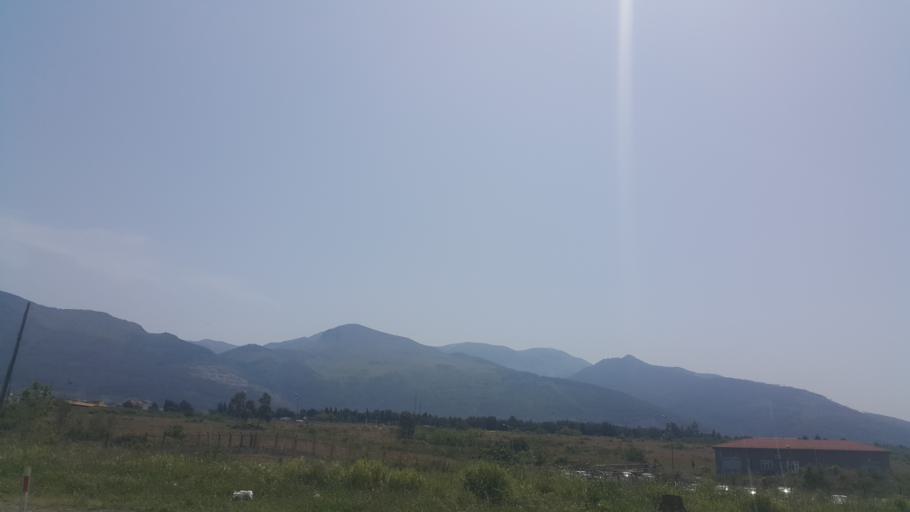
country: TR
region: Hatay
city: Denizciler
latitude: 36.6362
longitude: 36.2083
